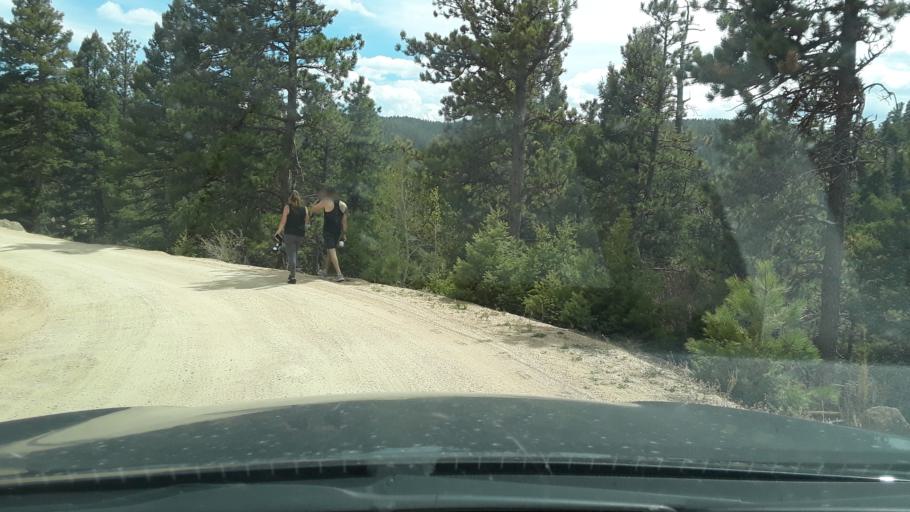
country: US
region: Colorado
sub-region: El Paso County
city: Palmer Lake
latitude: 39.0701
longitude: -104.9410
